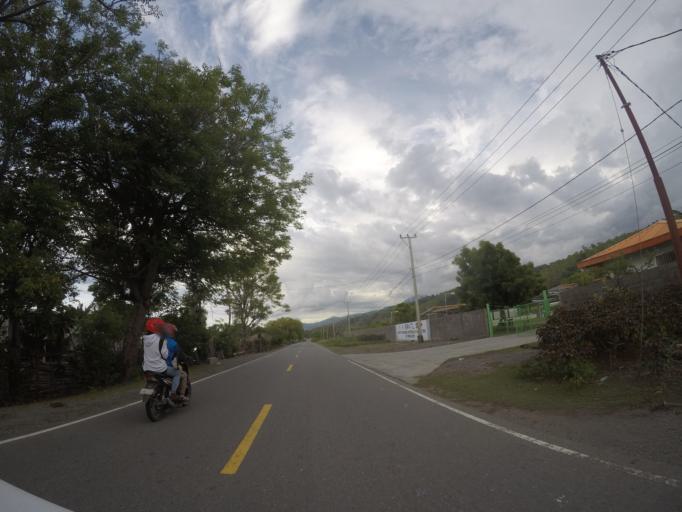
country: TL
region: Liquica
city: Maubara
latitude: -8.6065
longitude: 125.2647
